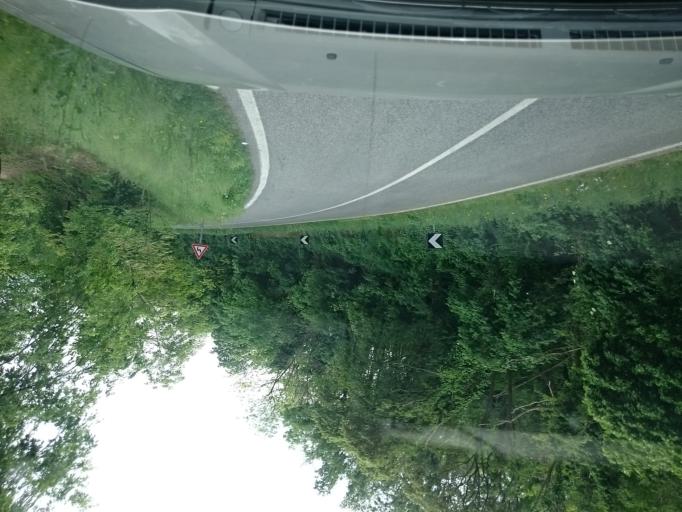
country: IT
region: Veneto
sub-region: Provincia di Padova
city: Baone
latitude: 45.2628
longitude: 11.6926
